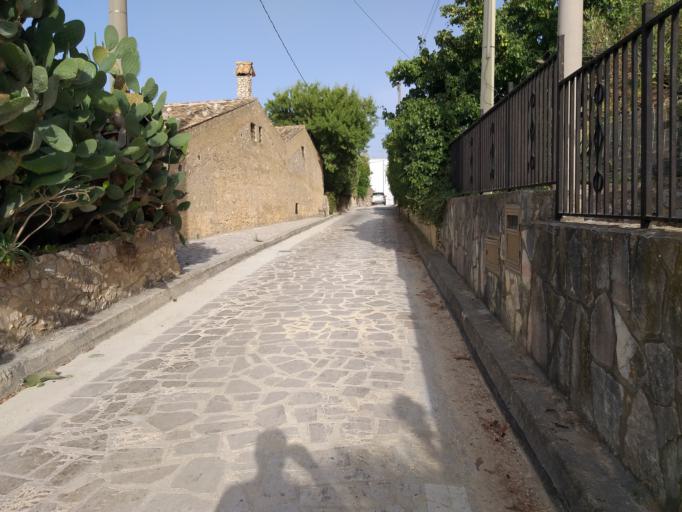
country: IT
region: Sicily
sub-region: Trapani
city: Castelluzzo
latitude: 38.0711
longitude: 12.8162
